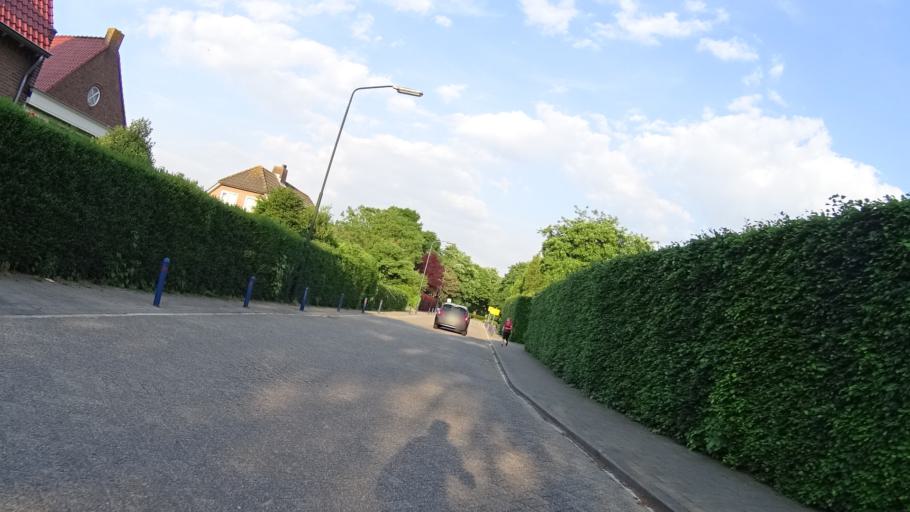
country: NL
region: North Brabant
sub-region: Gemeente Heusden
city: Heusden
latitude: 51.7271
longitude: 5.1358
